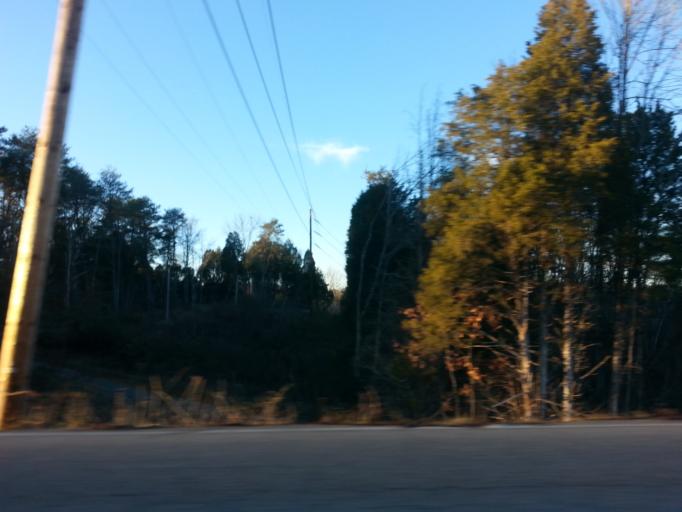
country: US
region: Tennessee
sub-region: Knox County
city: Mascot
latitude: 35.9823
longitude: -83.8100
